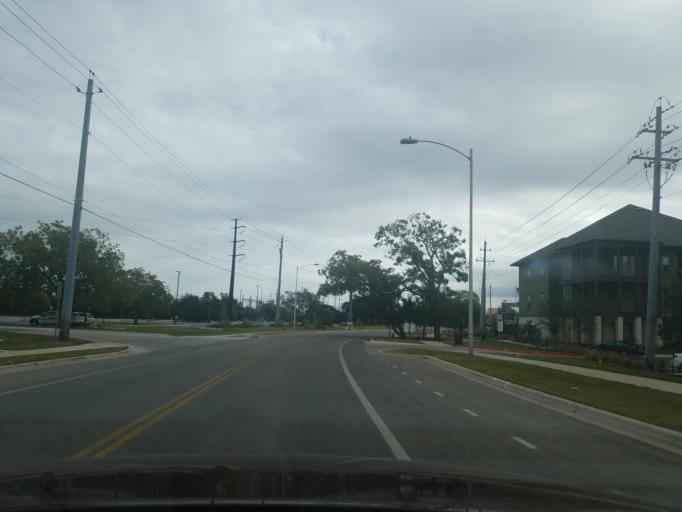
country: US
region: Texas
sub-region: Williamson County
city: Anderson Mill
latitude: 30.4780
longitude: -97.7850
